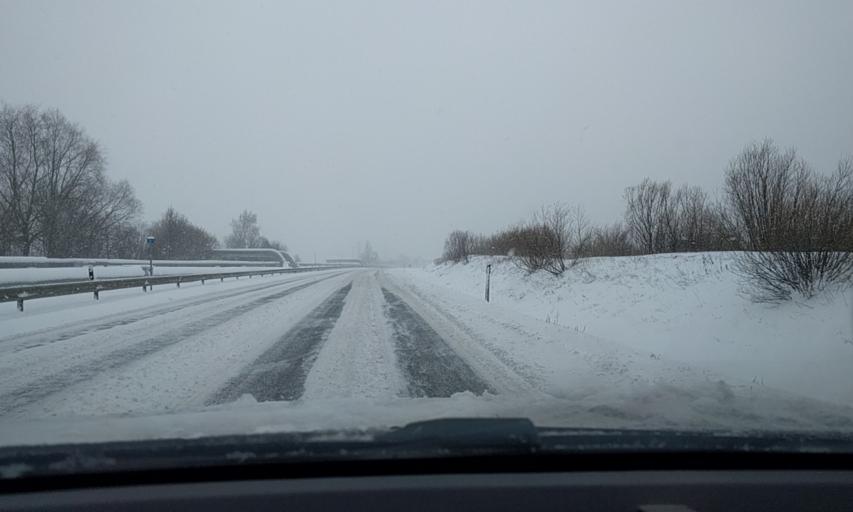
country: EE
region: Harju
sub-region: Maardu linn
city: Maardu
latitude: 59.4741
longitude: 24.9813
